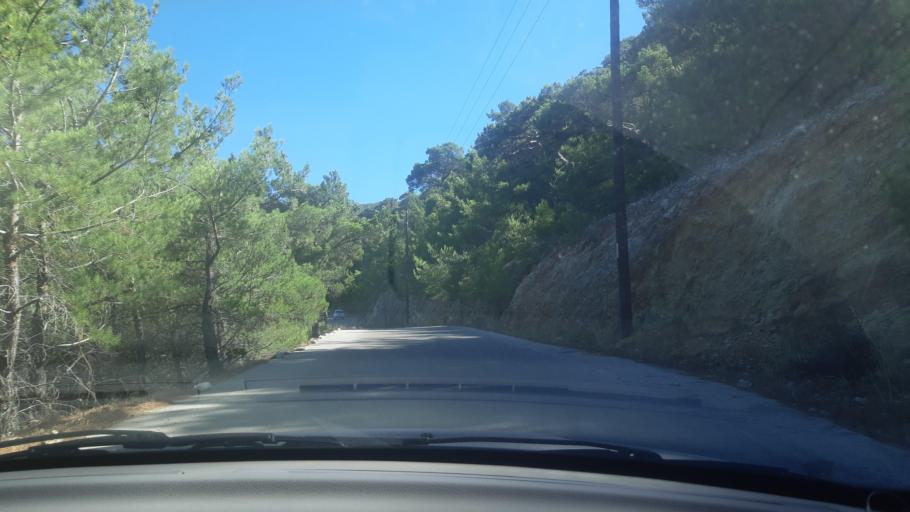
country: GR
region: South Aegean
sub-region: Nomos Dodekanisou
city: Karpathos
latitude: 35.5825
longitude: 27.1792
